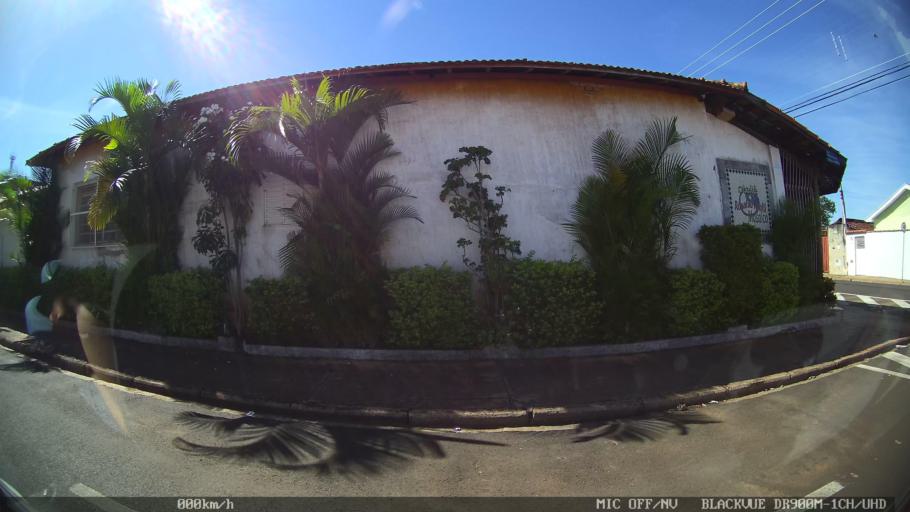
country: BR
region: Sao Paulo
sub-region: Franca
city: Franca
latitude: -20.5470
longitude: -47.3901
